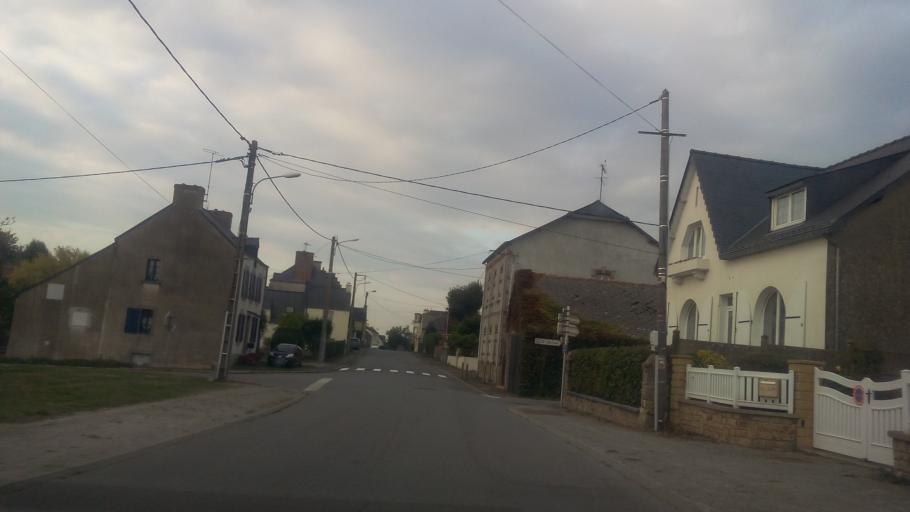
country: FR
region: Brittany
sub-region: Departement du Morbihan
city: Peillac
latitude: 47.7121
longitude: -2.2154
